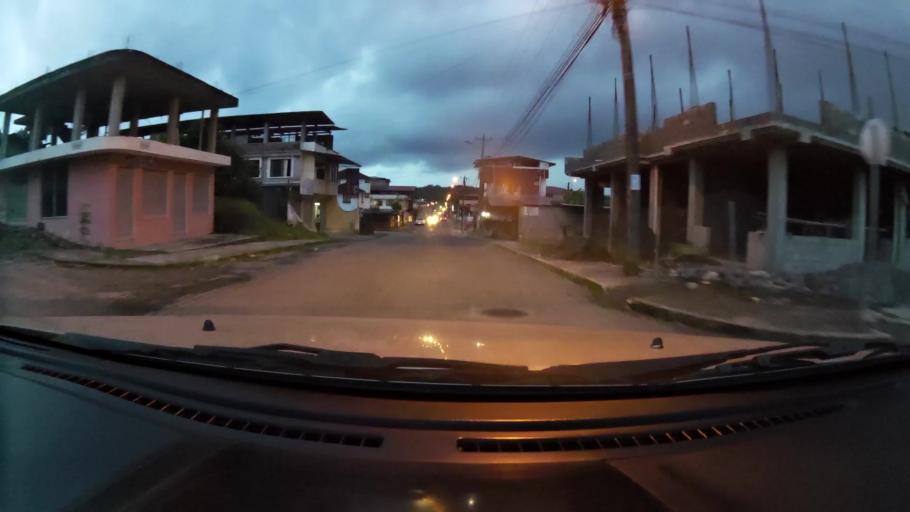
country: EC
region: Pastaza
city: Puyo
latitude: -1.4790
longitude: -78.0058
